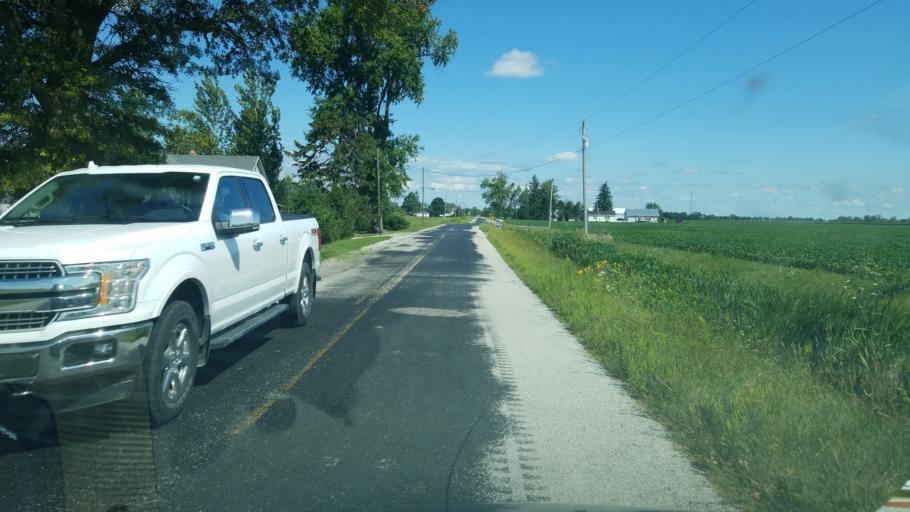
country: US
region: Ohio
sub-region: Henry County
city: Deshler
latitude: 41.2682
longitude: -83.8438
